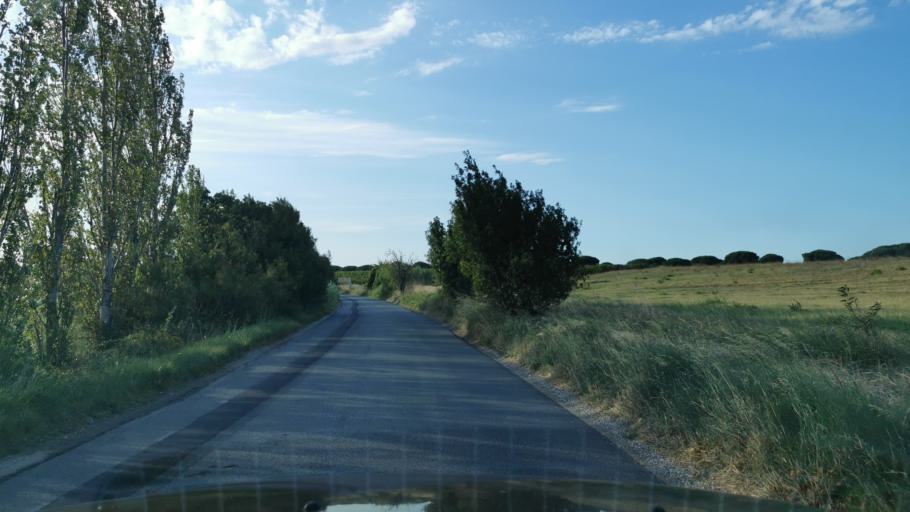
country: FR
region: Languedoc-Roussillon
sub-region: Departement de l'Aude
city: Narbonne
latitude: 43.1458
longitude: 3.0142
